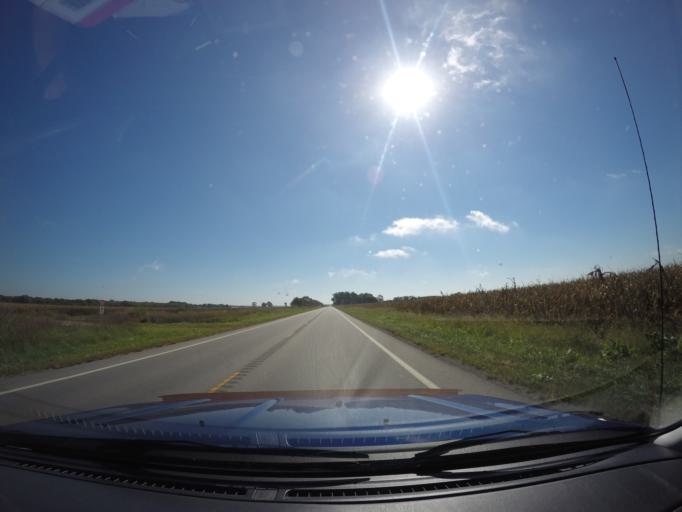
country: US
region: Kansas
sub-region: Shawnee County
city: Rossville
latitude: 39.1202
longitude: -95.9193
